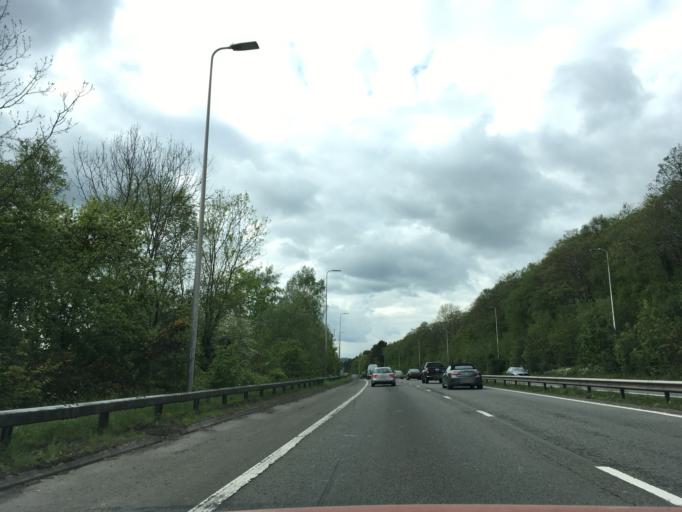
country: GB
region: Wales
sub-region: Caerphilly County Borough
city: Abertridwr
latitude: 51.5709
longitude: -3.2797
